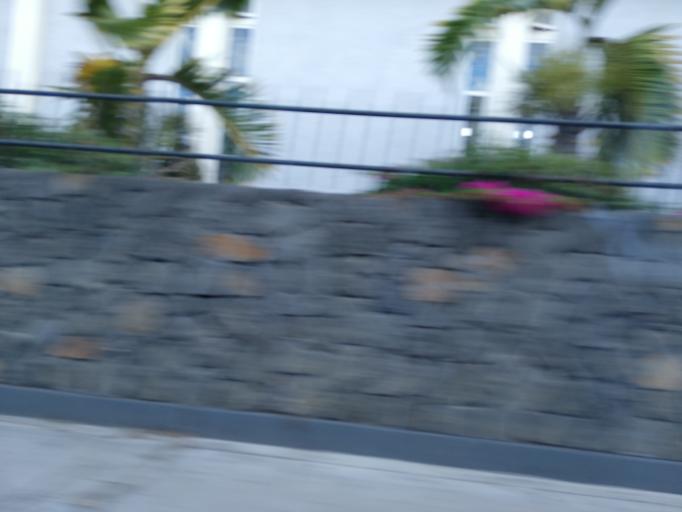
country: MU
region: Plaines Wilhems
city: Ebene
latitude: -20.2335
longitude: 57.4577
